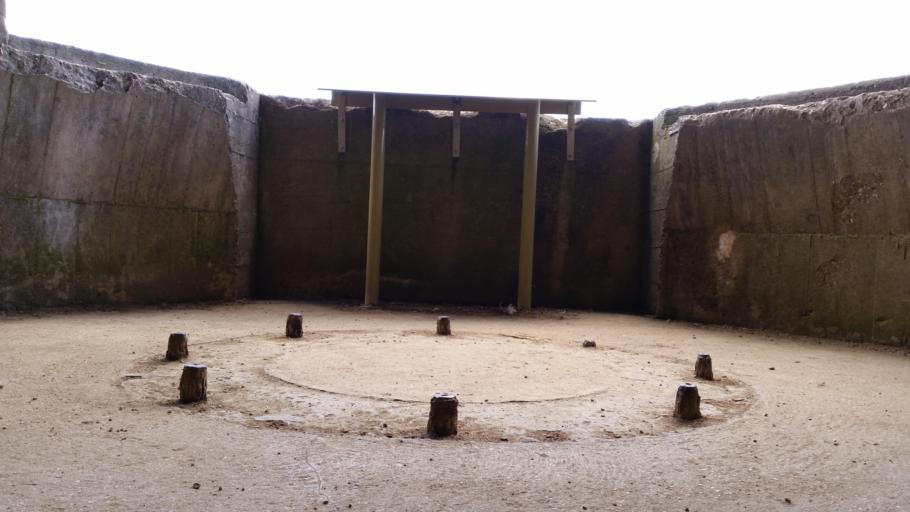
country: FR
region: Lower Normandy
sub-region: Departement de la Manche
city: Sainte-Mere-Eglise
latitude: 49.4621
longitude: -1.3068
